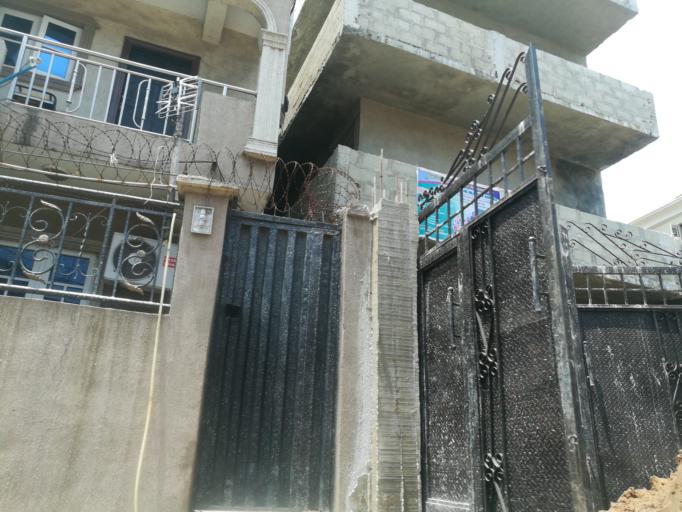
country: NG
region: Lagos
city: Lagos
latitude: 6.4530
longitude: 3.3952
